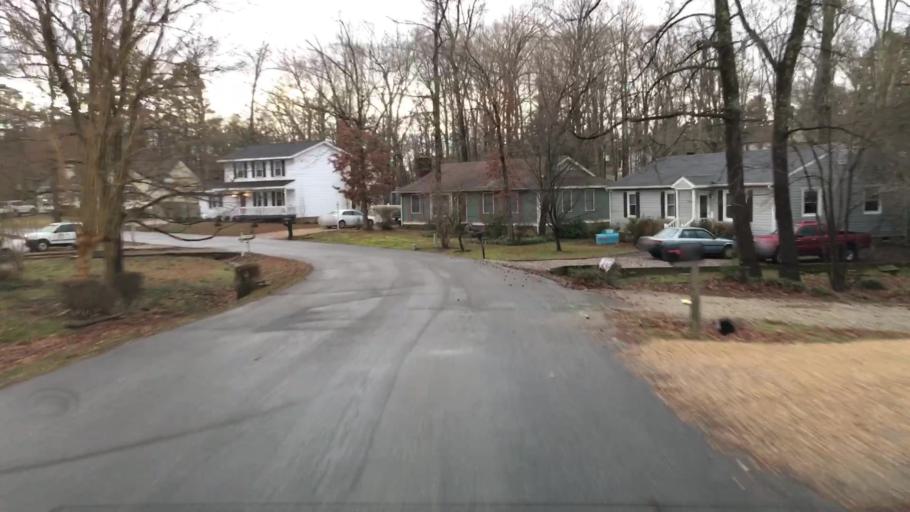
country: US
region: Virginia
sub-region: Chesterfield County
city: Bon Air
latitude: 37.5173
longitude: -77.6183
